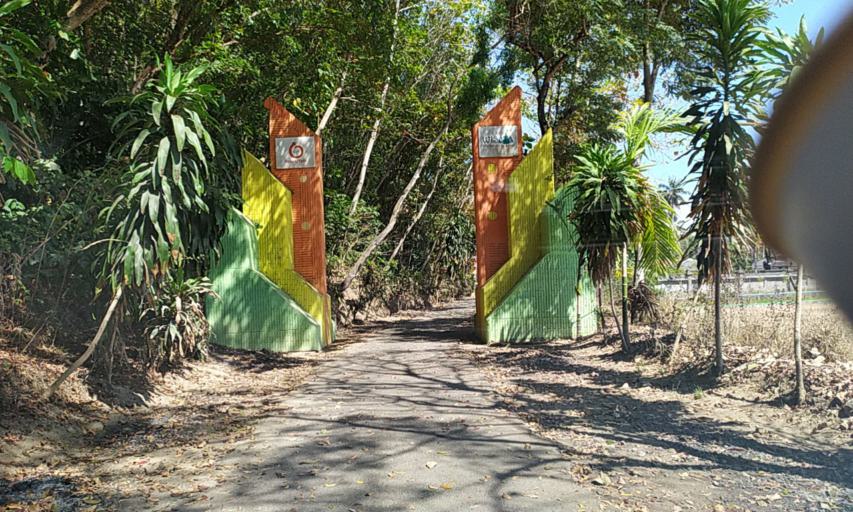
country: ID
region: Central Java
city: Adipala
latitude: -7.6811
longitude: 109.1855
